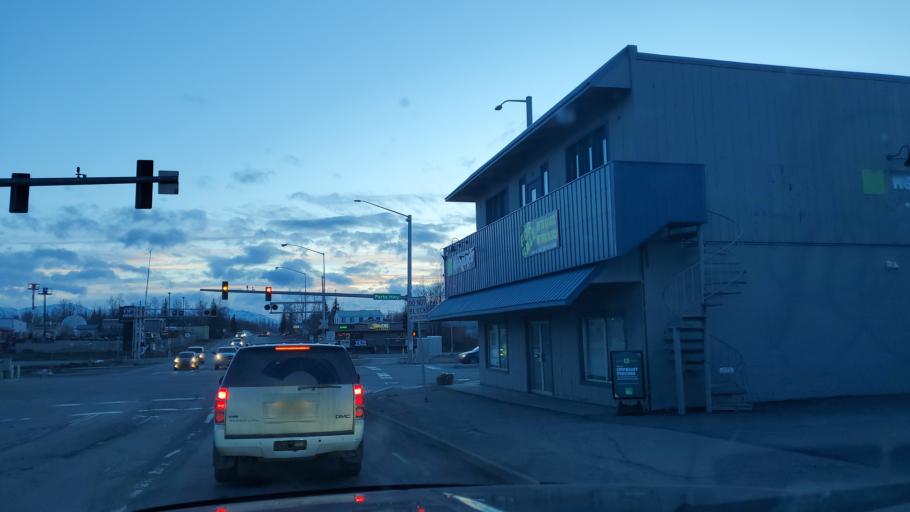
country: US
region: Alaska
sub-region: Matanuska-Susitna Borough
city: Wasilla
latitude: 61.5813
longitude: -149.4416
